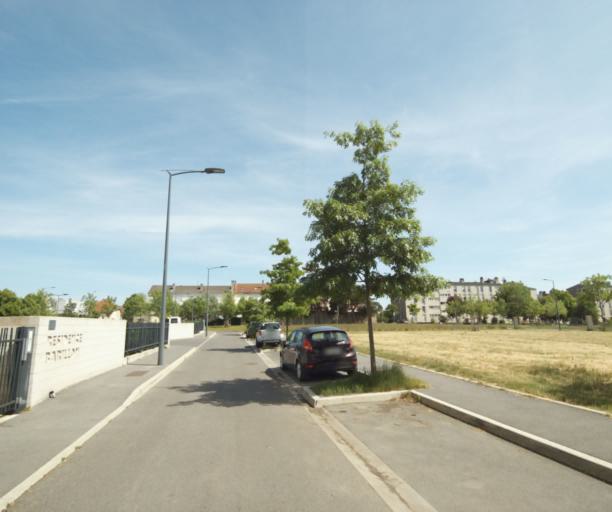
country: FR
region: Champagne-Ardenne
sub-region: Departement des Ardennes
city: Prix-les-Mezieres
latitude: 49.7649
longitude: 4.6894
